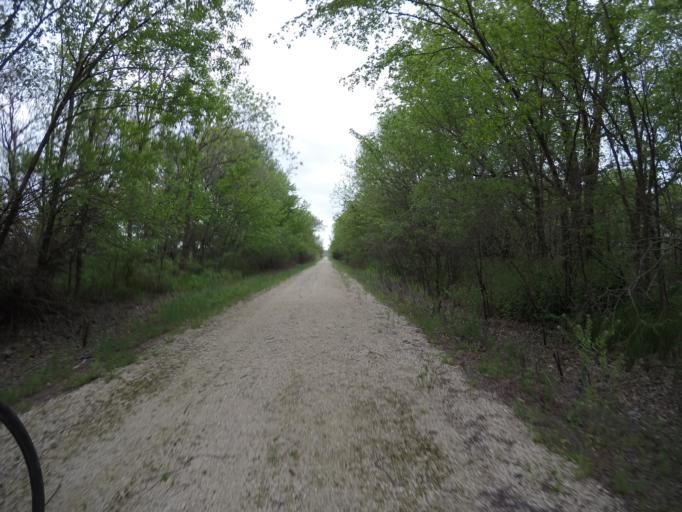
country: US
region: Nebraska
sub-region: Gage County
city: Wymore
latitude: 40.1525
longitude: -96.6415
